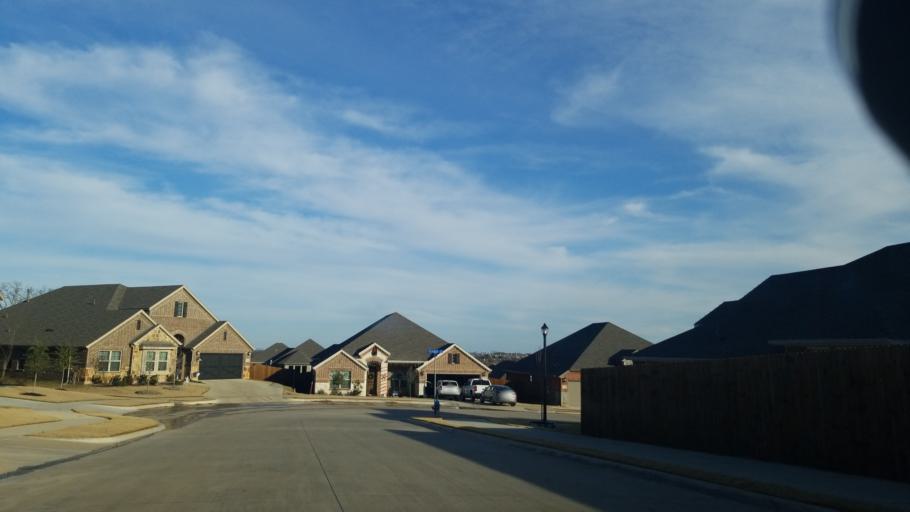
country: US
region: Texas
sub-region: Denton County
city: Corinth
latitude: 33.1469
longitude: -97.0767
